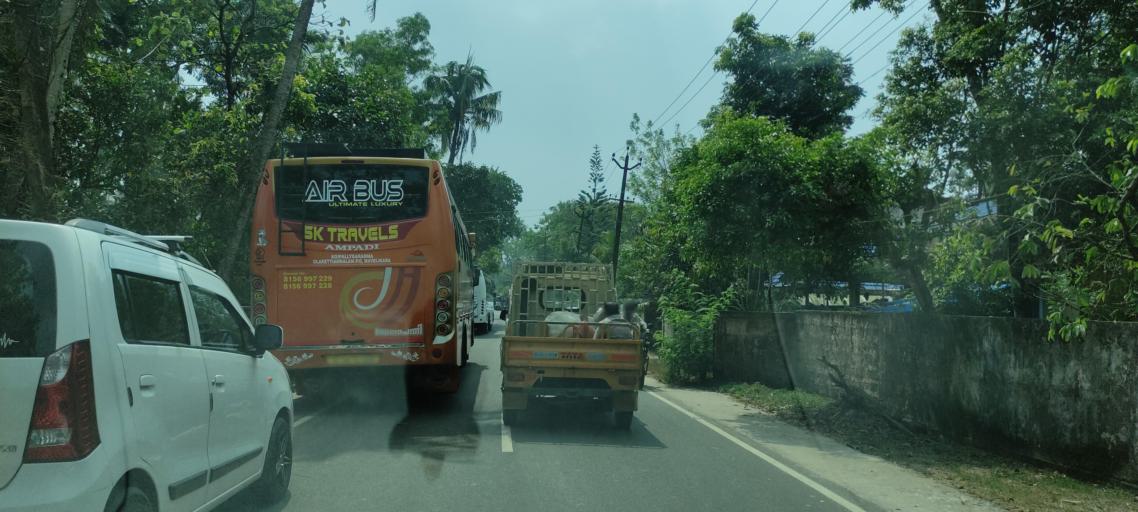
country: IN
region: Kerala
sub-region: Alappuzha
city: Shertallai
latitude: 9.5911
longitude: 76.3389
